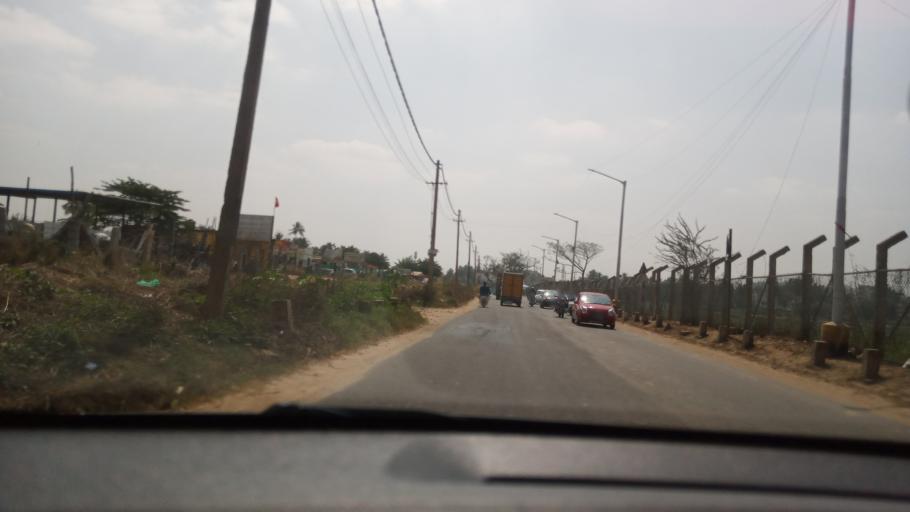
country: IN
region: Karnataka
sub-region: Bangalore Rural
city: Hoskote
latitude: 12.9485
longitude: 77.7459
